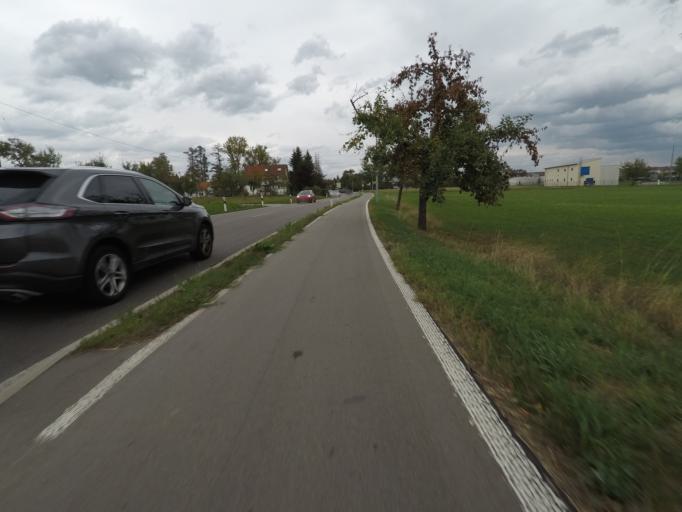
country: DE
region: Baden-Wuerttemberg
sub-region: Regierungsbezirk Stuttgart
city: Leinfelden-Echterdingen
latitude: 48.6792
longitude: 9.1669
